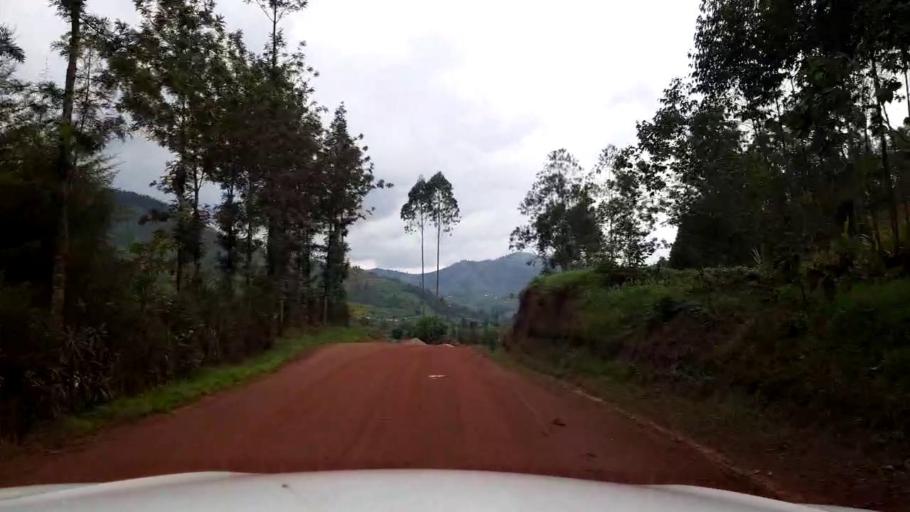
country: RW
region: Northern Province
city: Musanze
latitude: -1.6703
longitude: 29.8007
